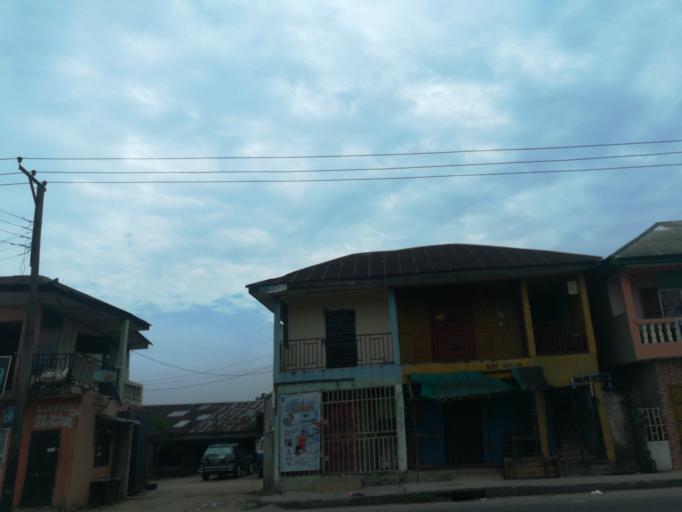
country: NG
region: Rivers
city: Port Harcourt
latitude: 4.8510
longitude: 6.9775
